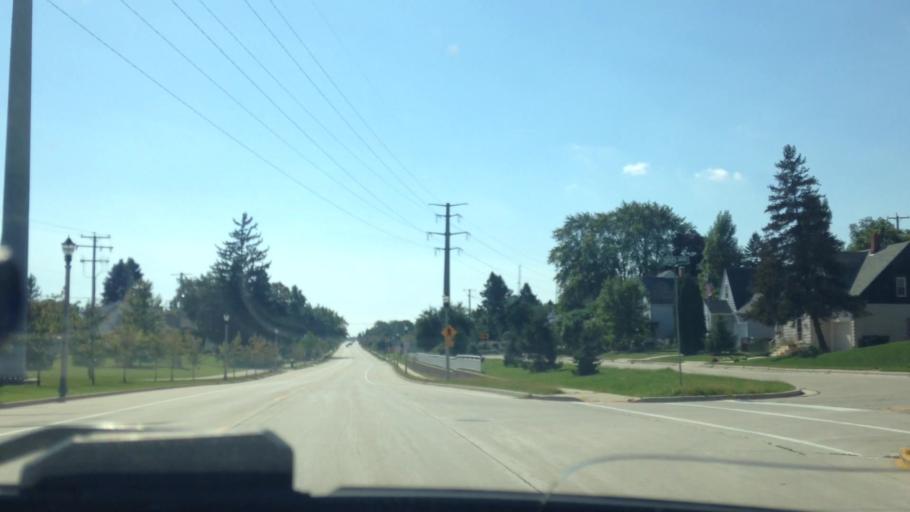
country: US
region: Wisconsin
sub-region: Ozaukee County
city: Port Washington
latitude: 43.3817
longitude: -87.8881
